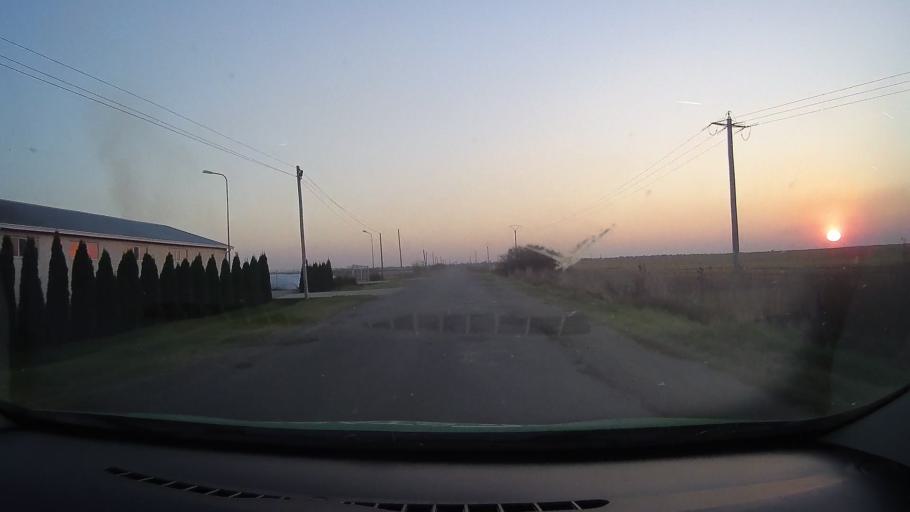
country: RO
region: Arad
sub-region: Comuna Olari
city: Olari
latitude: 46.3719
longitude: 21.5317
